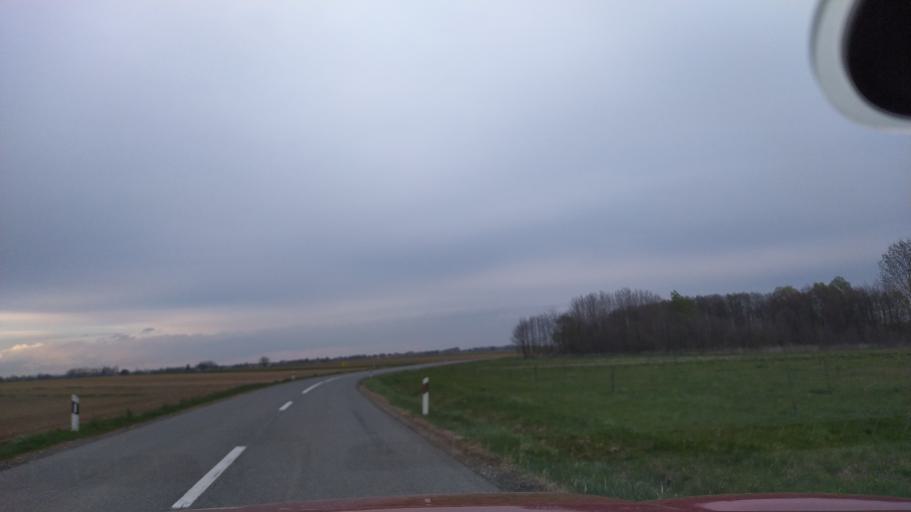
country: HR
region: Varazdinska
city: Ludbreg
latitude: 46.2483
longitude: 16.5603
